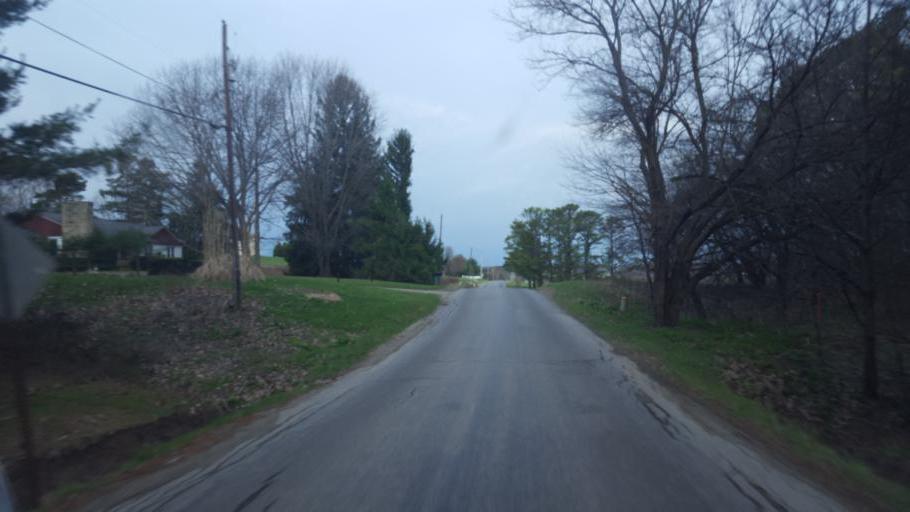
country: US
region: Ohio
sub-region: Sandusky County
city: Bellville
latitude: 40.5864
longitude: -82.5703
